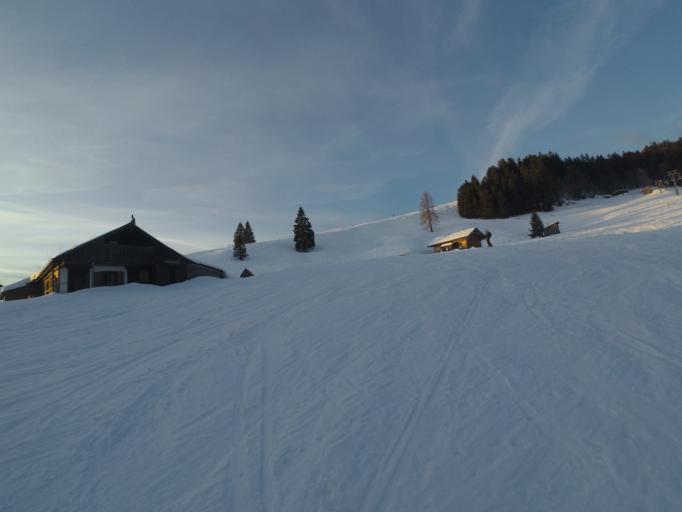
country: AT
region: Salzburg
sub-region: Politischer Bezirk Hallein
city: Krispl
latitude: 47.7208
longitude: 13.2193
